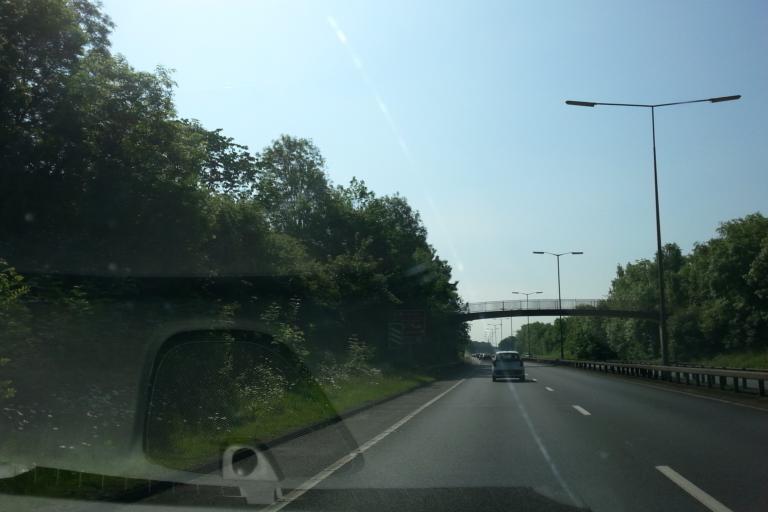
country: GB
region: England
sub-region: Peterborough
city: Marholm
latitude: 52.5694
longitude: -0.2922
